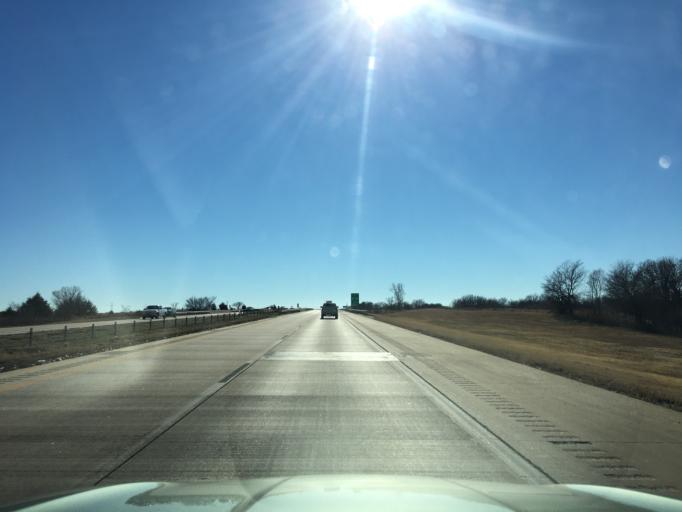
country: US
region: Oklahoma
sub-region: Noble County
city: Perry
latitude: 36.4361
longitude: -97.3271
